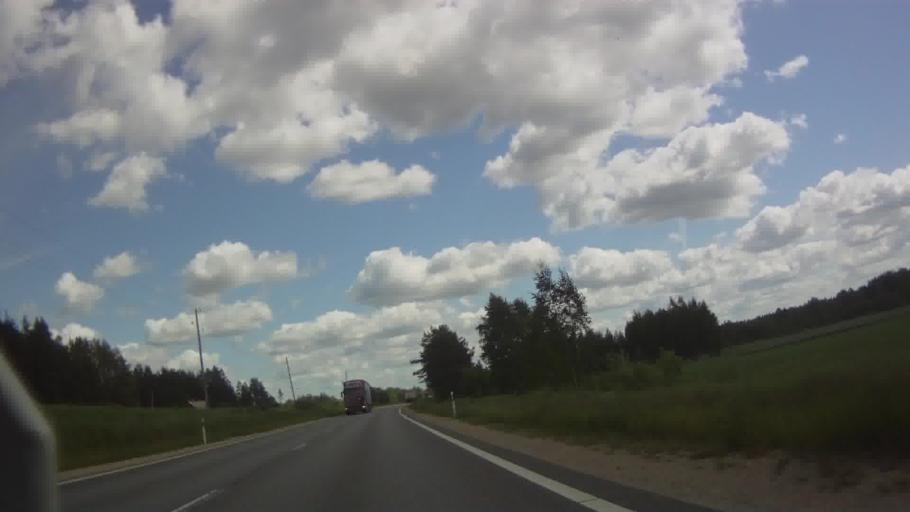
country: LV
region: Jekabpils Rajons
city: Jekabpils
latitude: 56.5390
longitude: 26.0606
